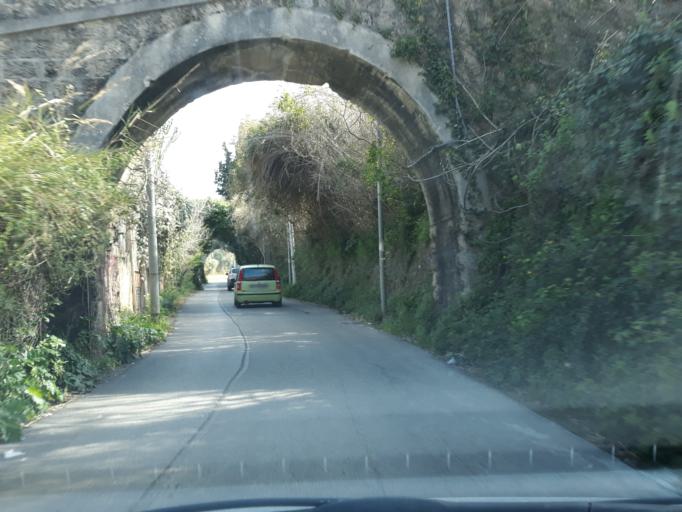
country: IT
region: Sicily
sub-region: Palermo
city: Monreale
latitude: 38.0731
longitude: 13.2827
